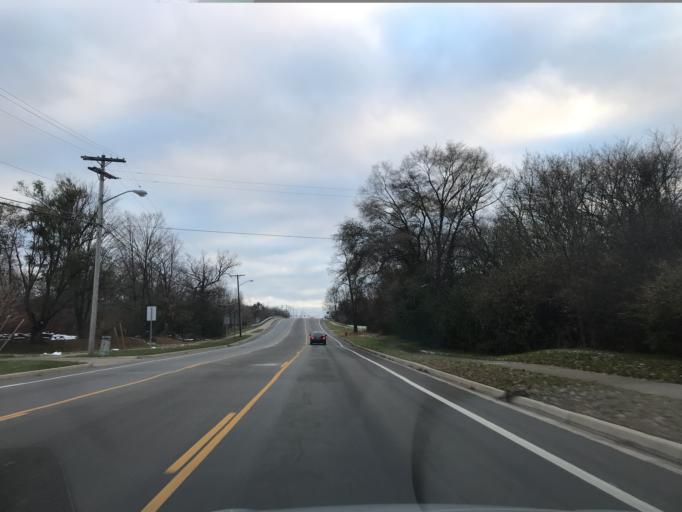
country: US
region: Michigan
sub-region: Washtenaw County
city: Ann Arbor
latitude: 42.2351
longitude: -83.7000
